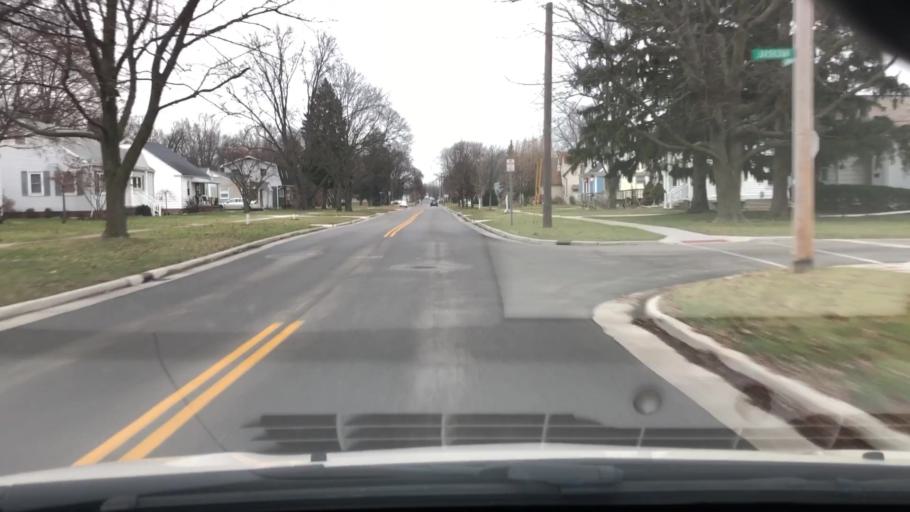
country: US
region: Ohio
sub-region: Lucas County
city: Maumee
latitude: 41.5699
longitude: -83.6497
